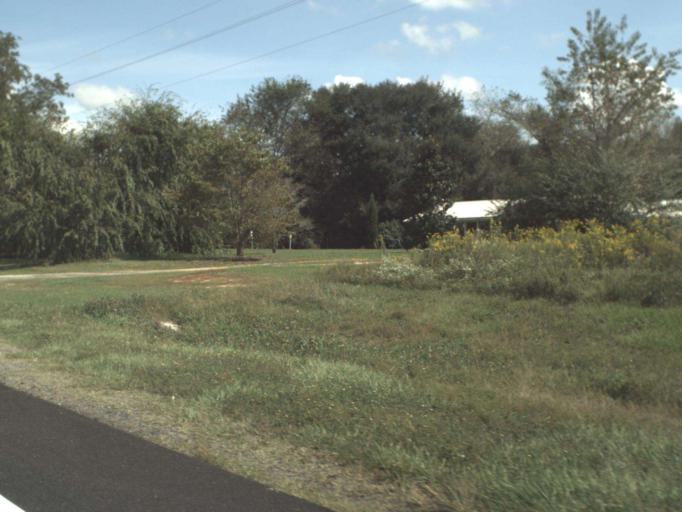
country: US
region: Florida
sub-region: Jackson County
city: Graceville
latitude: 30.9799
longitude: -85.4082
